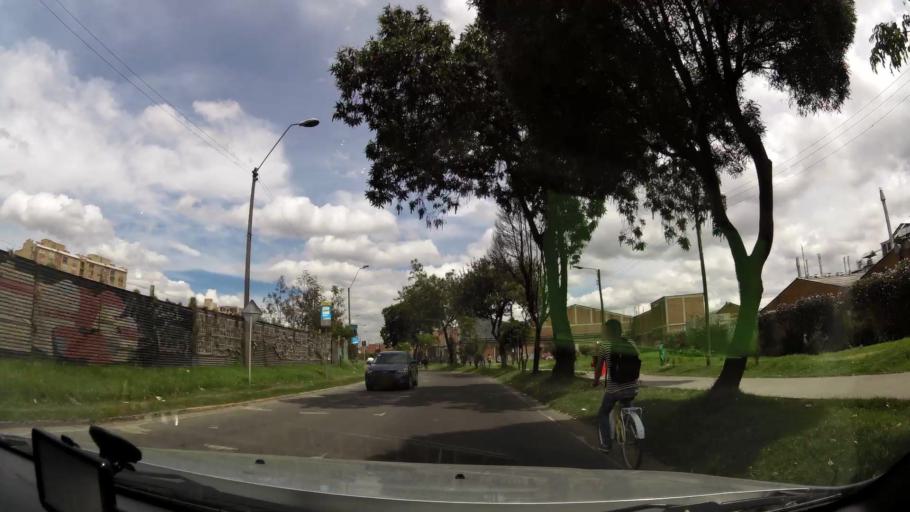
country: CO
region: Bogota D.C.
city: Bogota
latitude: 4.6464
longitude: -74.1325
